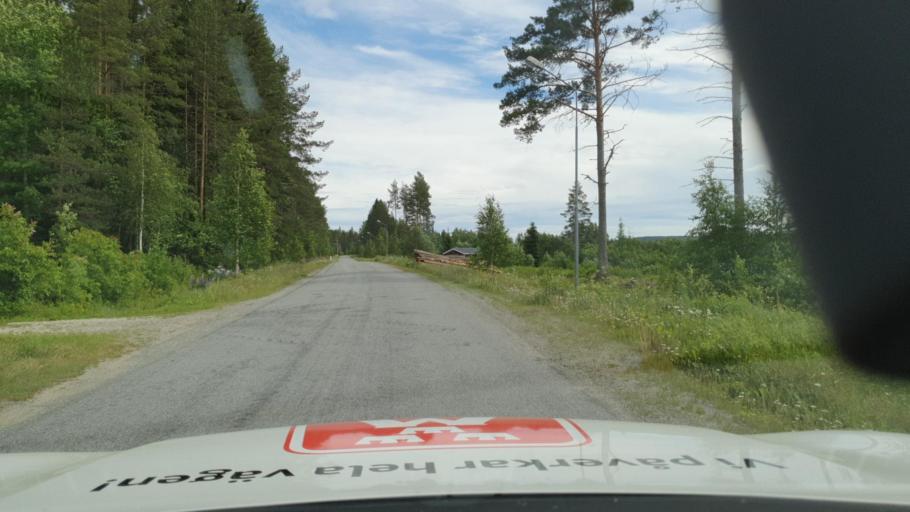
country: SE
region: Vaesterbotten
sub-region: Skelleftea Kommun
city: Burtraesk
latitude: 64.4851
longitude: 20.5088
